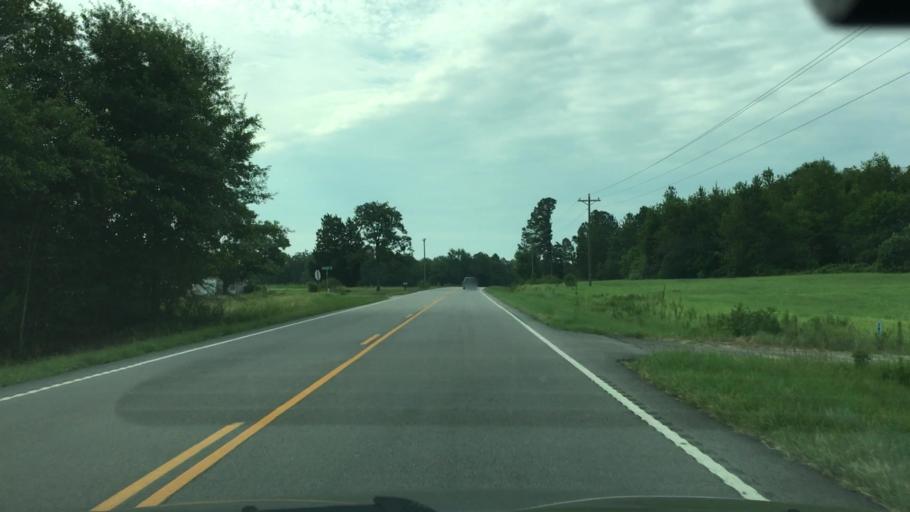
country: US
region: South Carolina
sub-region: Lexington County
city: Batesburg
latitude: 33.7437
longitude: -81.5190
